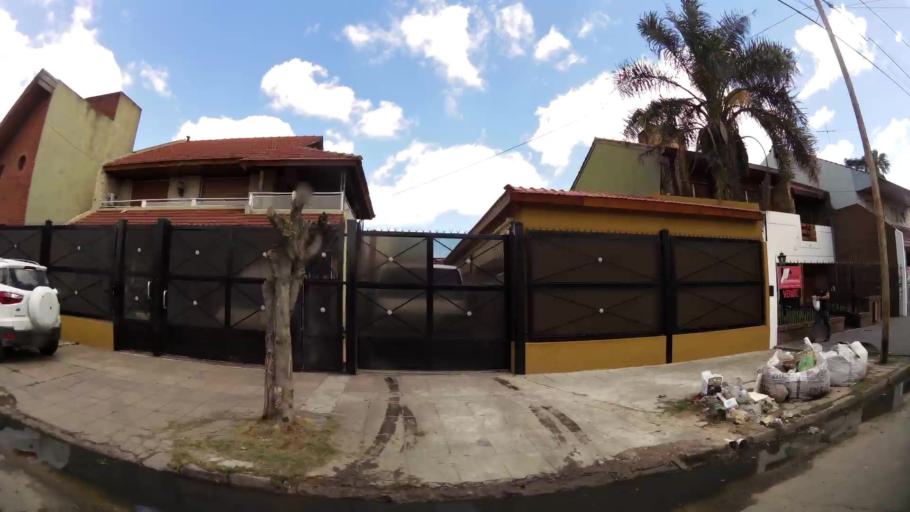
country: AR
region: Buenos Aires
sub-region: Partido de Lanus
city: Lanus
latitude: -34.7106
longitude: -58.4202
